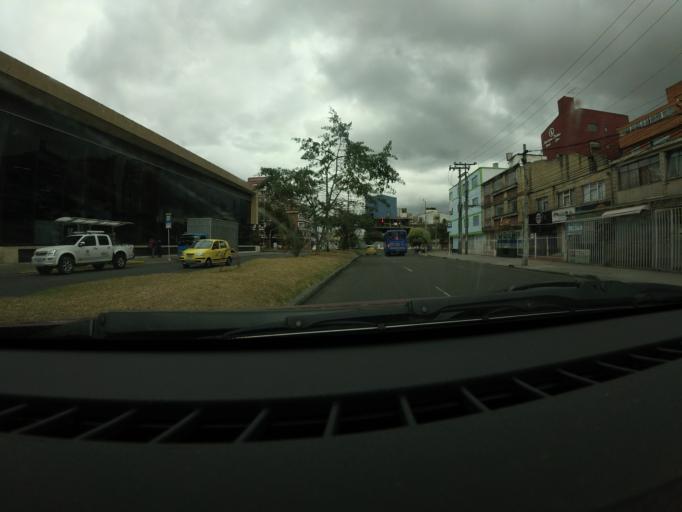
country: CO
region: Bogota D.C.
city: Bogota
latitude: 4.6323
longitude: -74.0899
